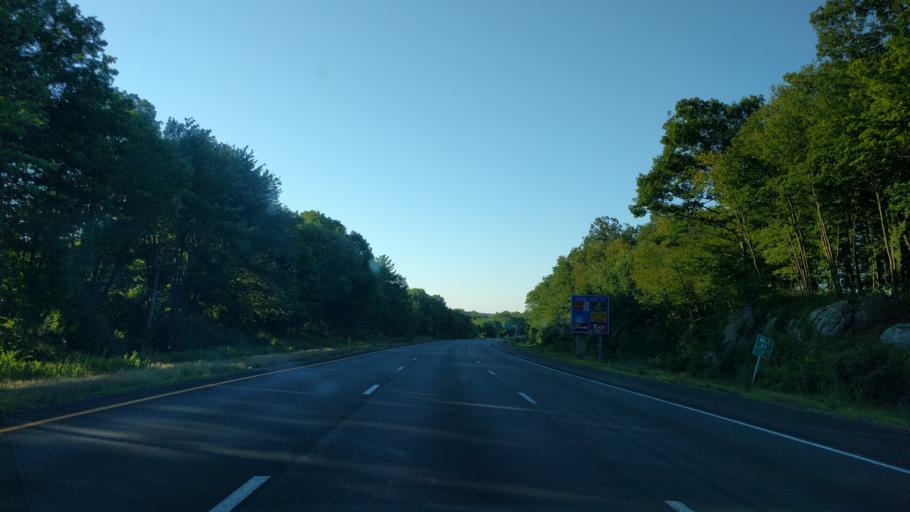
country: US
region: Massachusetts
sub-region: Worcester County
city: Milford
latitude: 42.1587
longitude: -71.4924
